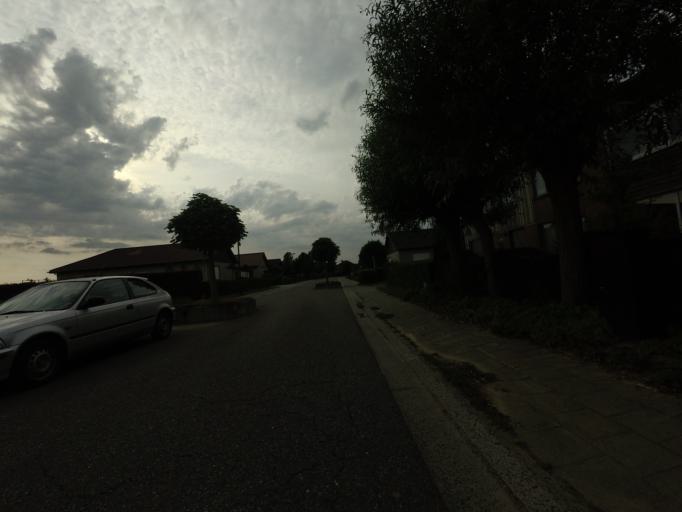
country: BE
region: Flanders
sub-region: Provincie Vlaams-Brabant
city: Meise
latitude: 50.9514
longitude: 4.3385
